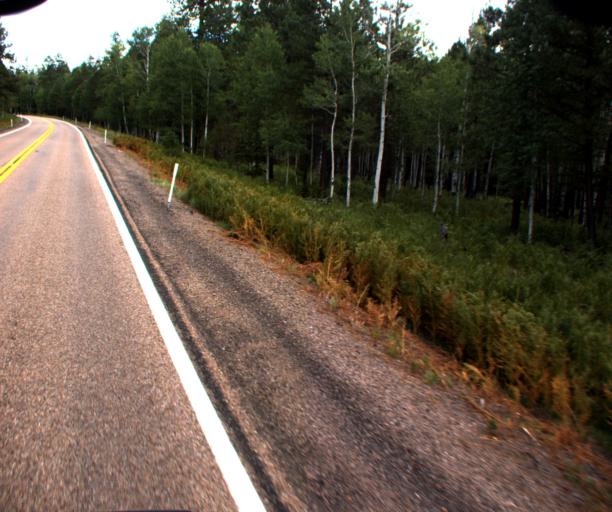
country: US
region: Arizona
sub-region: Apache County
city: Eagar
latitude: 34.0292
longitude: -109.6287
